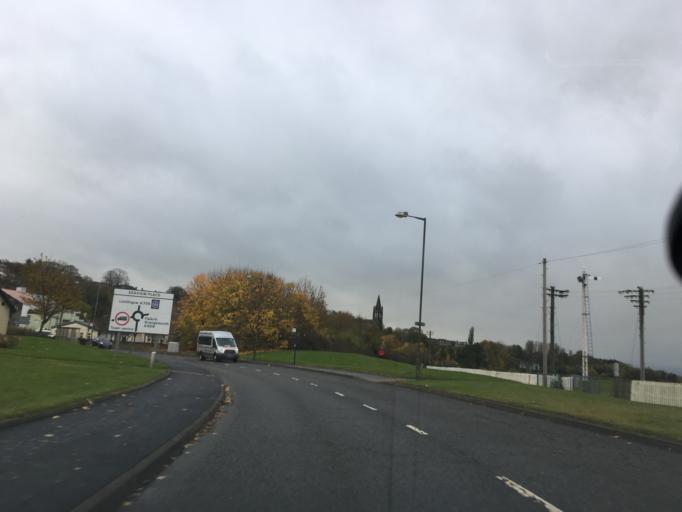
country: GB
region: Scotland
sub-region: Falkirk
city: Bo'ness
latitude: 56.0177
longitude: -3.6107
